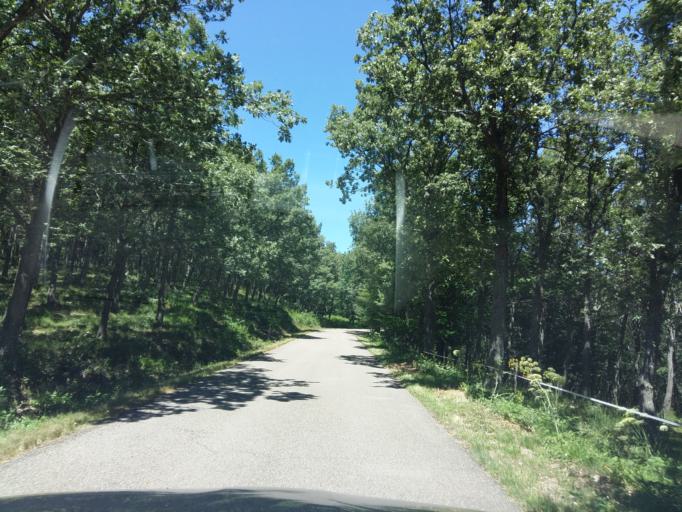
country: ES
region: Castille and Leon
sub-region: Provincia de Soria
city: Vozmediano
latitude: 41.8125
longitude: -1.8161
